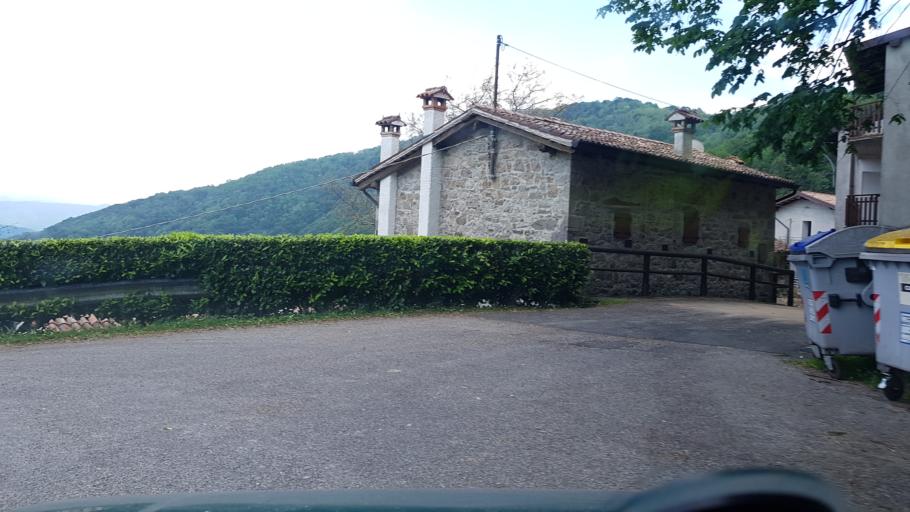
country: IT
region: Friuli Venezia Giulia
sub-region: Provincia di Udine
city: Pulfero
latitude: 46.1815
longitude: 13.4441
